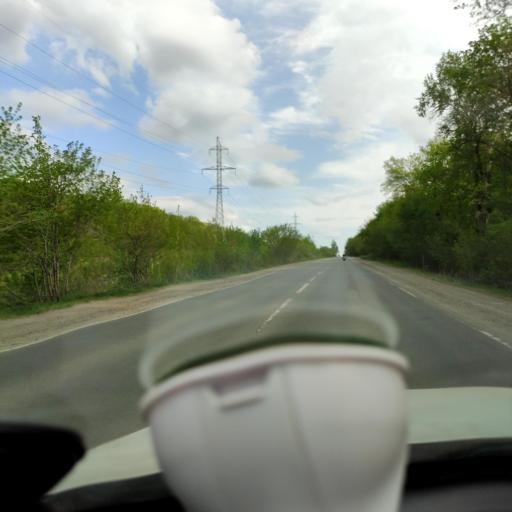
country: RU
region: Samara
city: Novosemeykino
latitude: 53.3452
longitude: 50.2440
